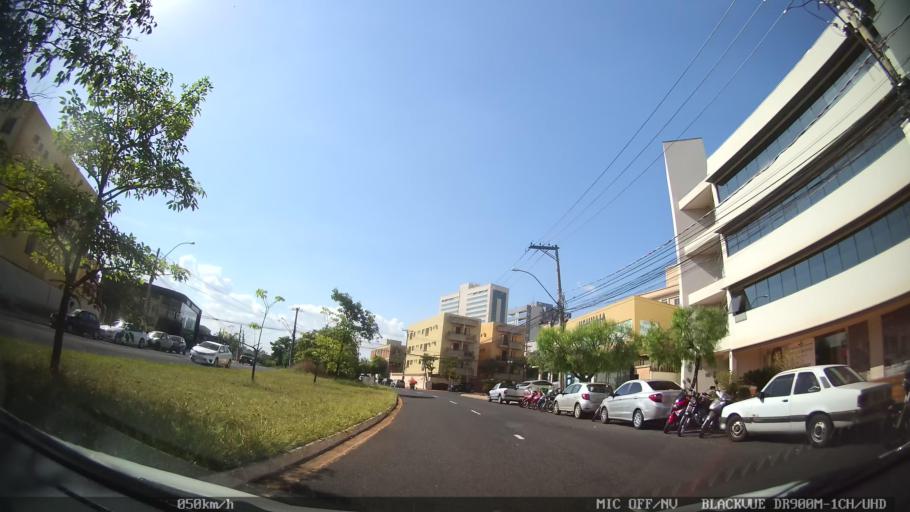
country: BR
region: Sao Paulo
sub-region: Ribeirao Preto
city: Ribeirao Preto
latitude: -21.2109
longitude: -47.8170
